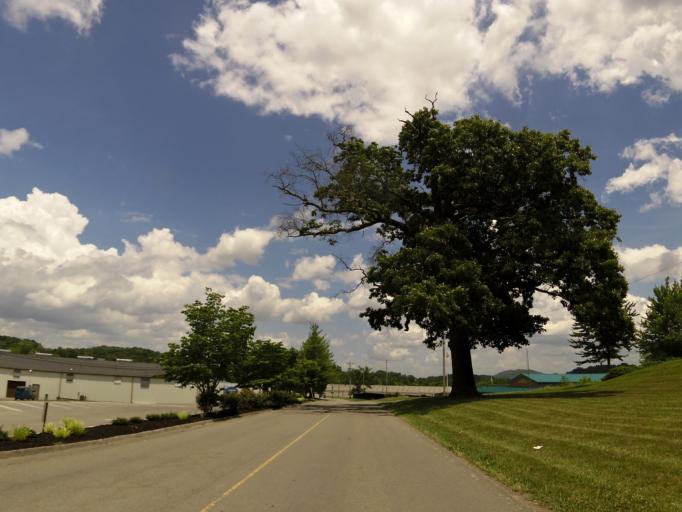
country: US
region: Tennessee
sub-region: Claiborne County
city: New Tazewell
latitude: 36.4413
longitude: -83.5940
